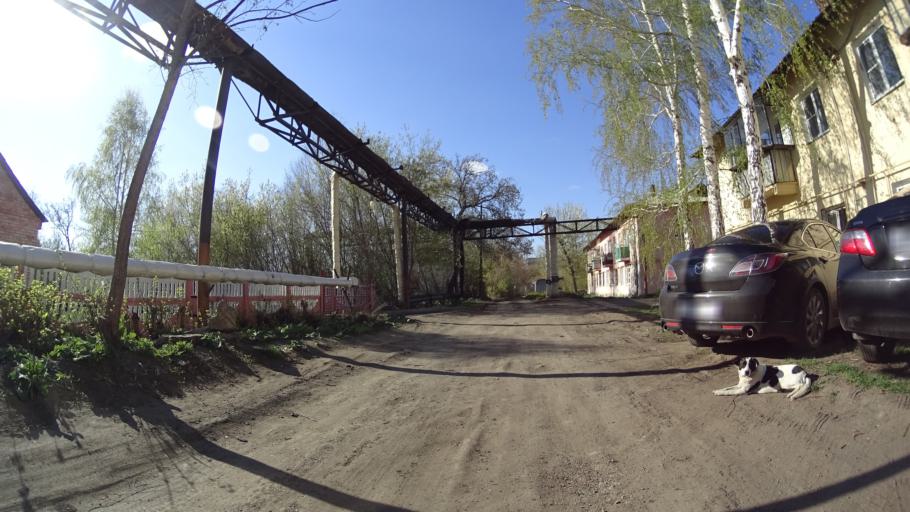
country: RU
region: Chelyabinsk
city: Troitsk
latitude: 54.1035
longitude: 61.5579
